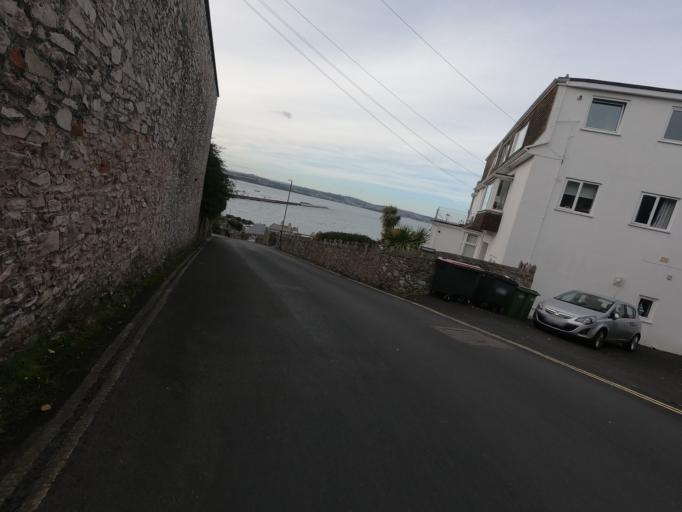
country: GB
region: England
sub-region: Borough of Torbay
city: Brixham
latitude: 50.3999
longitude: -3.4974
